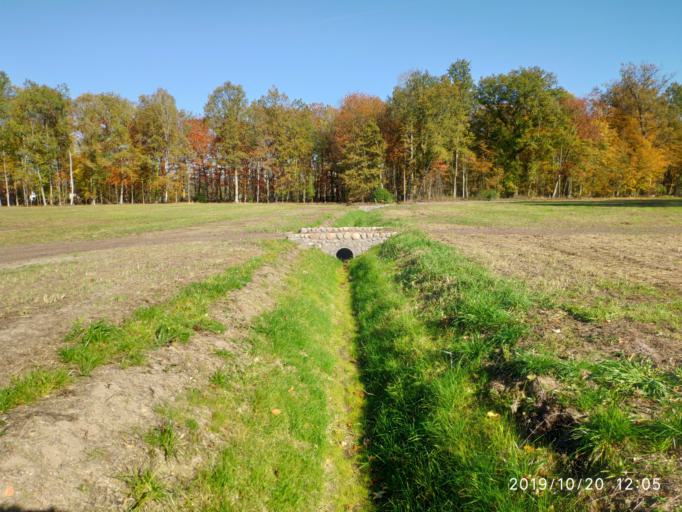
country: PL
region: Lubusz
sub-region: Zielona Gora
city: Zielona Gora
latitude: 51.8599
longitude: 15.5664
